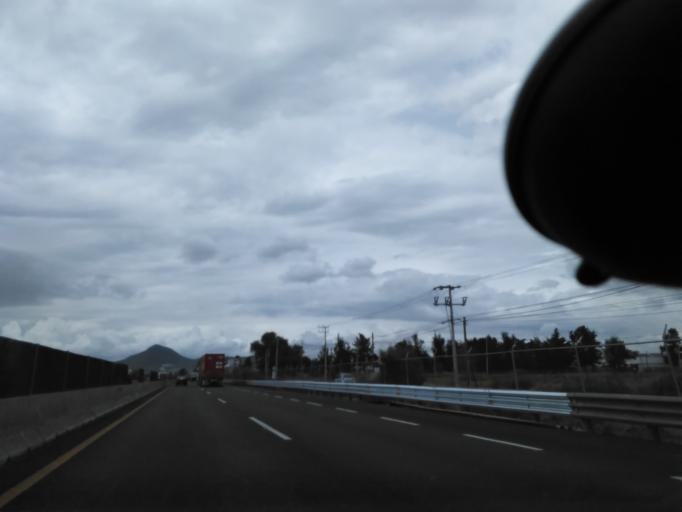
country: MX
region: Morelos
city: San Pedro Xalpa
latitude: 19.8159
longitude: -99.1981
